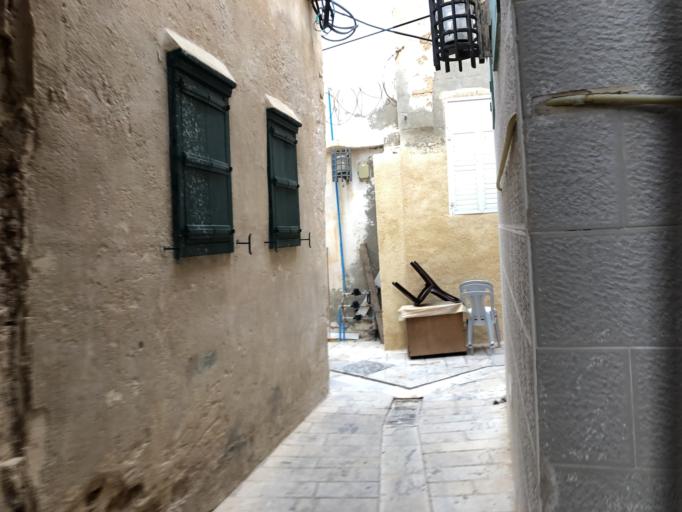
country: IL
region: Northern District
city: `Akko
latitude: 32.9235
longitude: 35.0686
